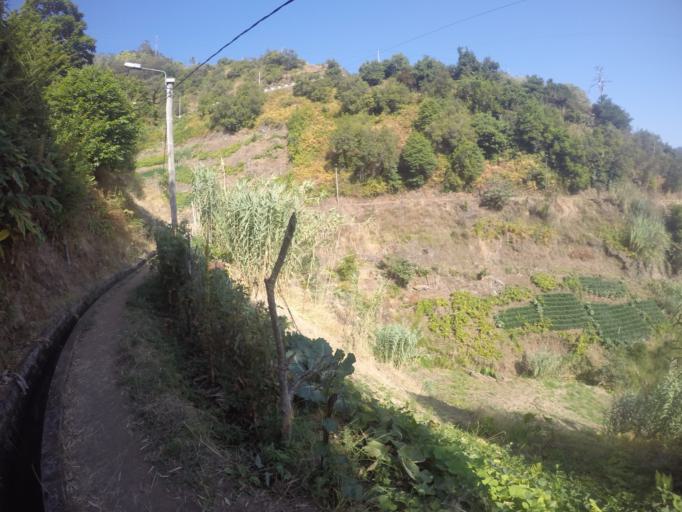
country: PT
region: Madeira
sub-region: Santana
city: Santana
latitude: 32.7635
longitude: -16.8244
